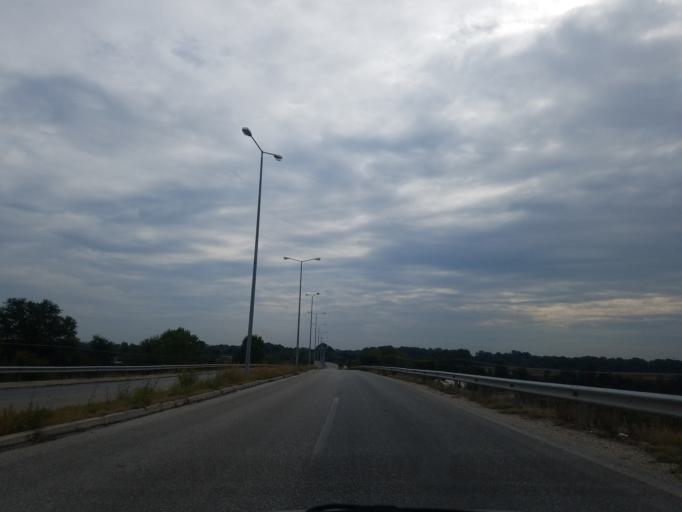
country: GR
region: Thessaly
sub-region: Trikala
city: Pyrgetos
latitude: 39.5201
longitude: 21.7576
